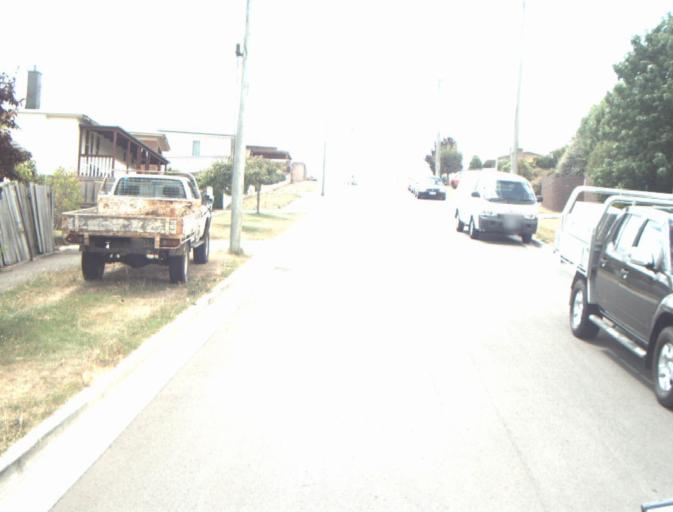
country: AU
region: Tasmania
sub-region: Launceston
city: Newnham
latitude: -41.4123
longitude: 147.1481
